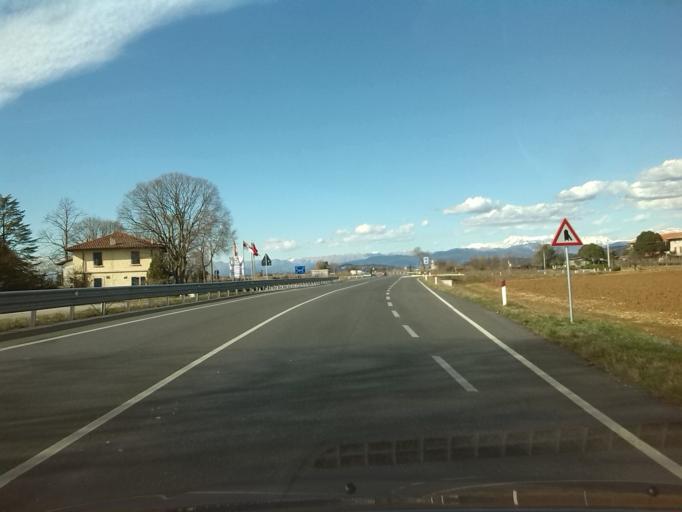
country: IT
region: Friuli Venezia Giulia
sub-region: Provincia di Gorizia
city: Mariano del Friuli
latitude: 45.9276
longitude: 13.4534
